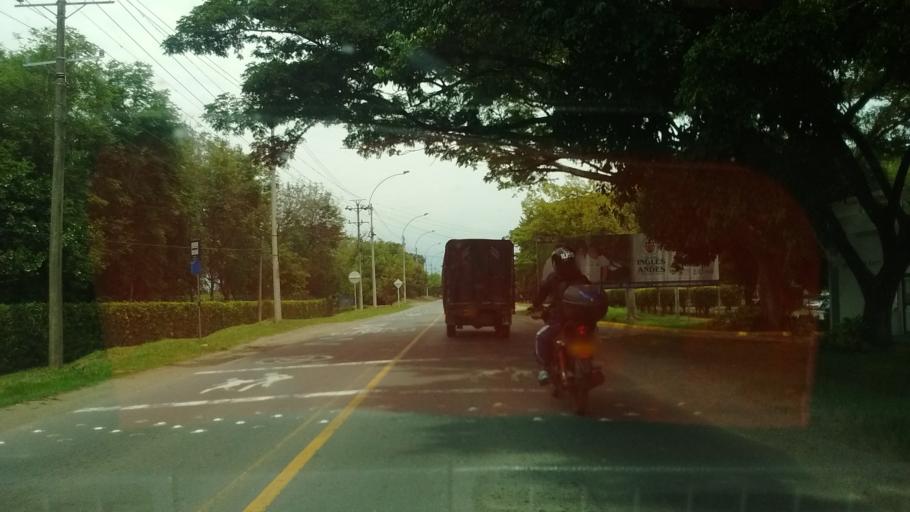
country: CO
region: Valle del Cauca
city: Jamundi
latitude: 3.3217
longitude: -76.4974
